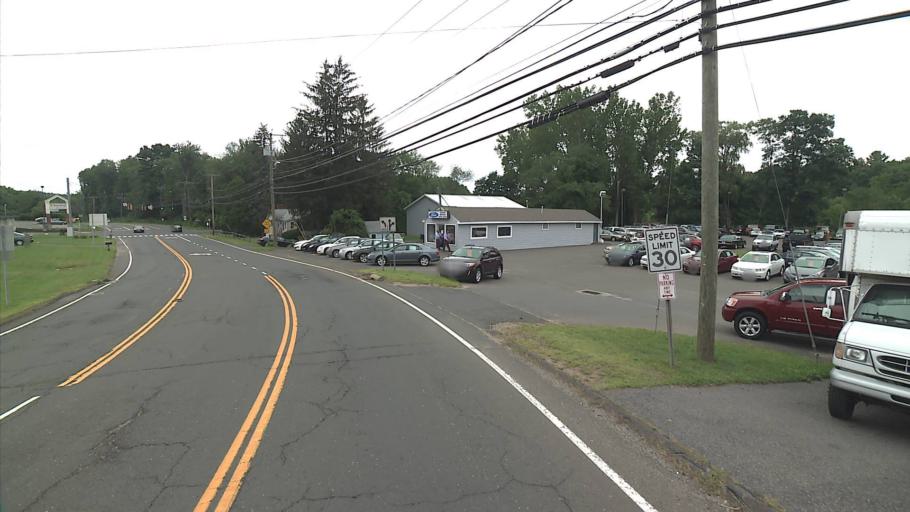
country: US
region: Connecticut
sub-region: Tolland County
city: Rockville
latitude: 41.8647
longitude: -72.4795
